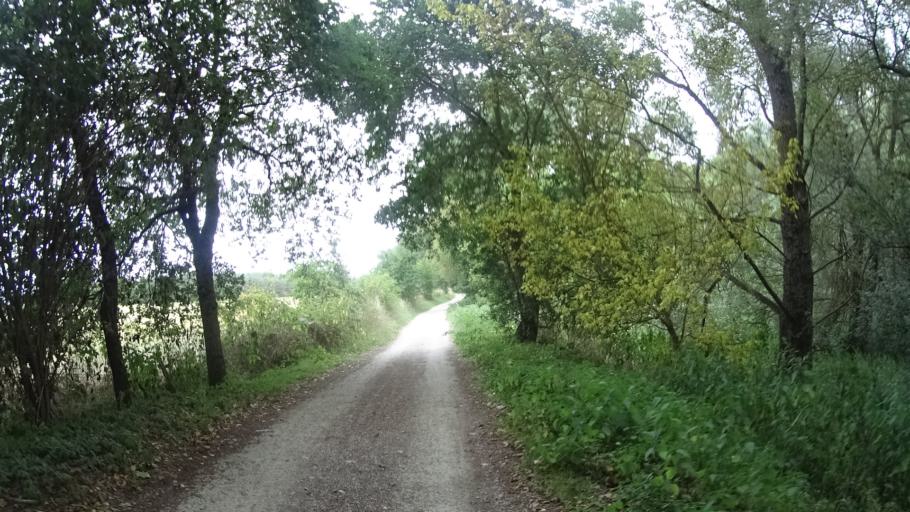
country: FR
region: Centre
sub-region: Departement du Loiret
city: Baule
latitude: 47.7923
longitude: 1.6775
